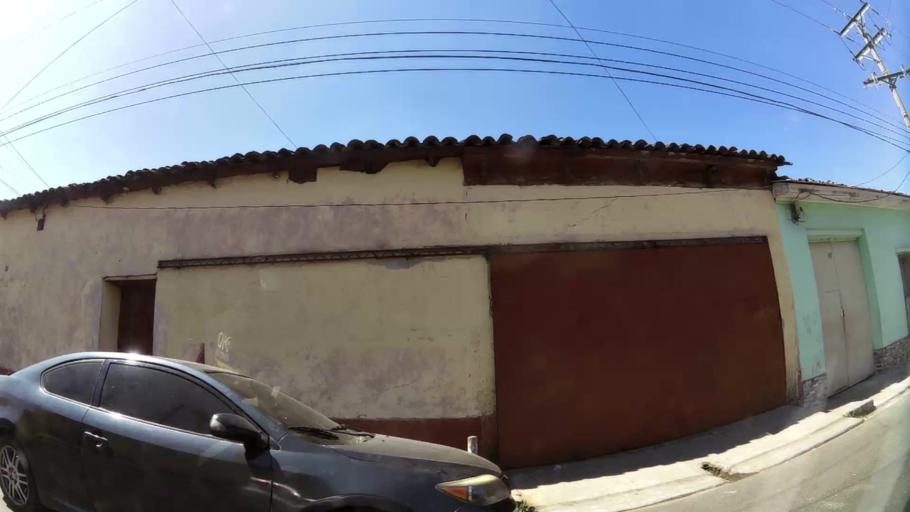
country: SV
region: Ahuachapan
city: Atiquizaya
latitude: 13.9754
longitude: -89.7546
